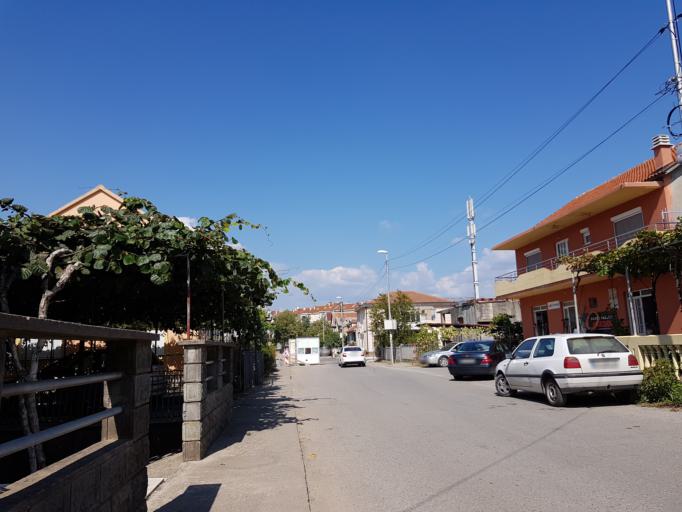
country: ME
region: Podgorica
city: Podgorica
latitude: 42.4299
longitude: 19.2771
